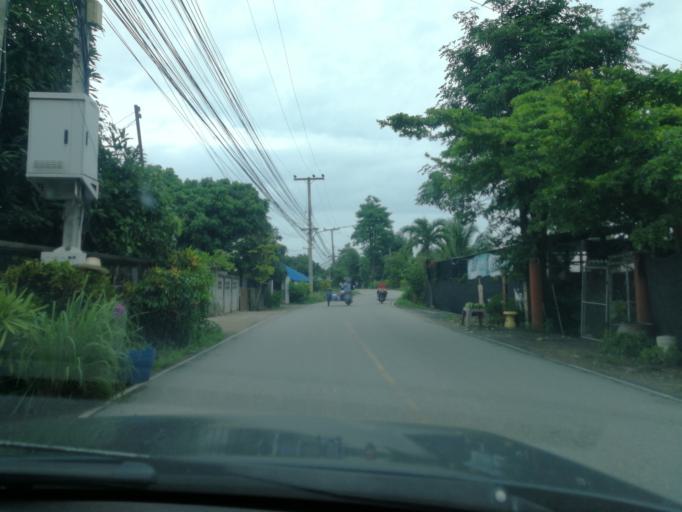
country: TH
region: Chiang Mai
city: San Pa Tong
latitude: 18.6034
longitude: 98.9070
